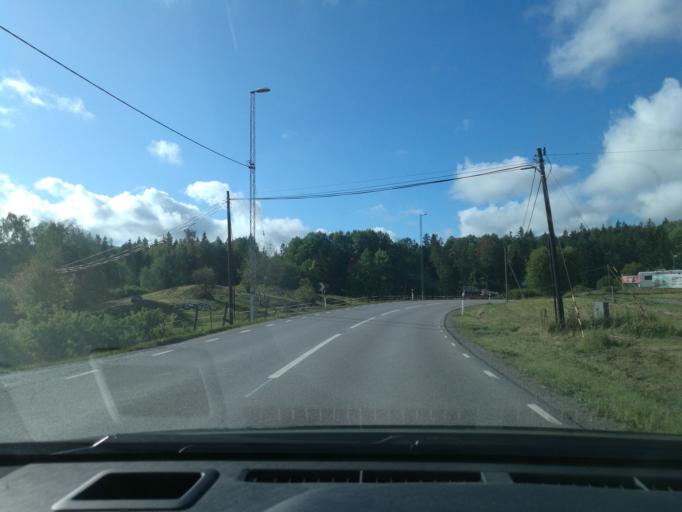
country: SE
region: Stockholm
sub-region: Upplands Vasby Kommun
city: Upplands Vaesby
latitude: 59.5308
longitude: 17.9895
